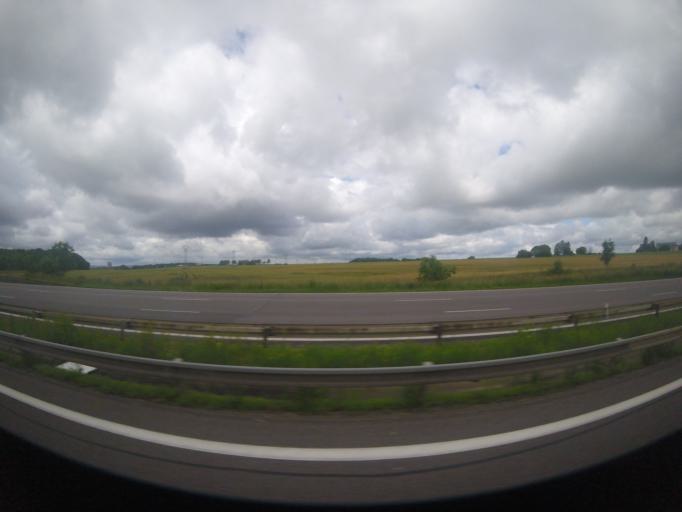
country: FR
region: Lorraine
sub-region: Departement de la Moselle
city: Saint-Julien-les-Metz
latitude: 49.1445
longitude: 6.2473
